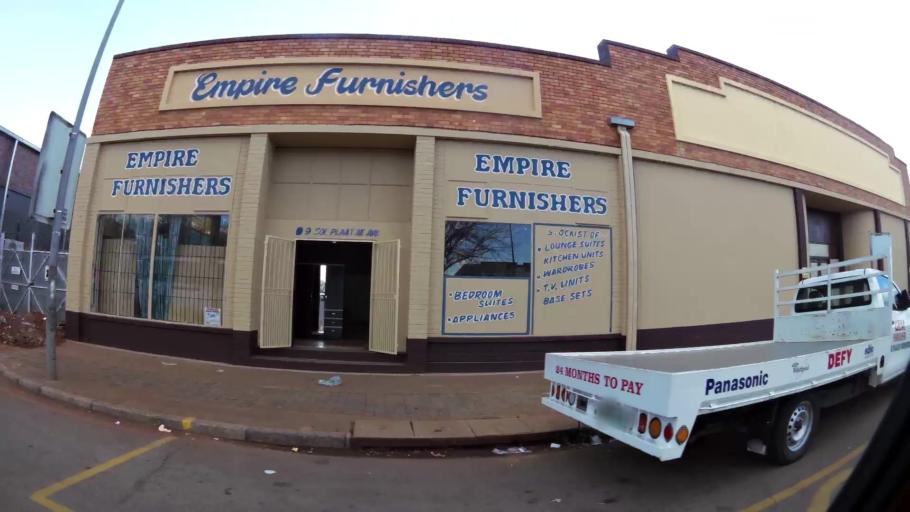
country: ZA
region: North-West
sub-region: Dr Kenneth Kaunda District Municipality
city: Potchefstroom
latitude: -26.7120
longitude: 27.0992
